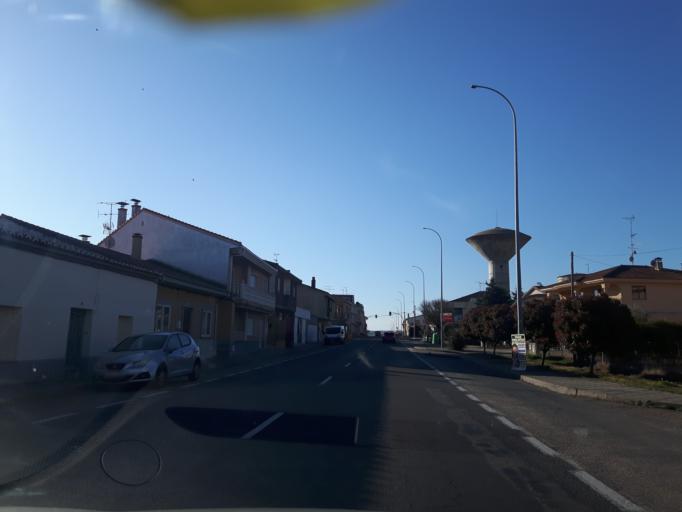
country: ES
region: Castille and Leon
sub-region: Provincia de Salamanca
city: Calvarrasa de Arriba
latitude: 40.9068
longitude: -5.5937
